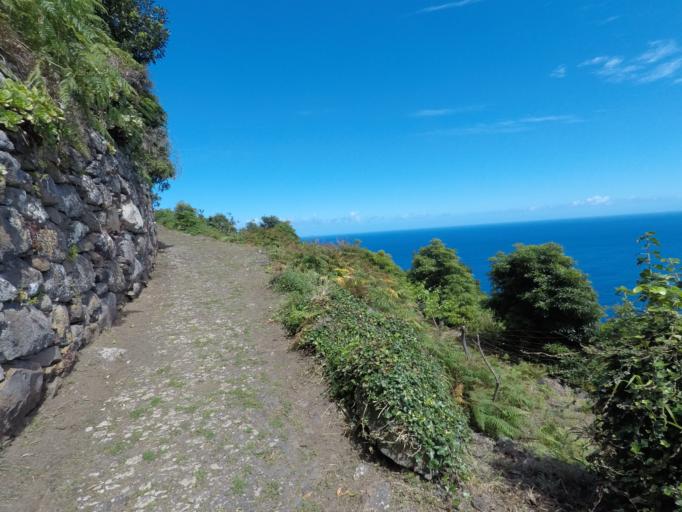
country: PT
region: Madeira
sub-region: Santana
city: Santana
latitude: 32.8255
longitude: -16.9630
